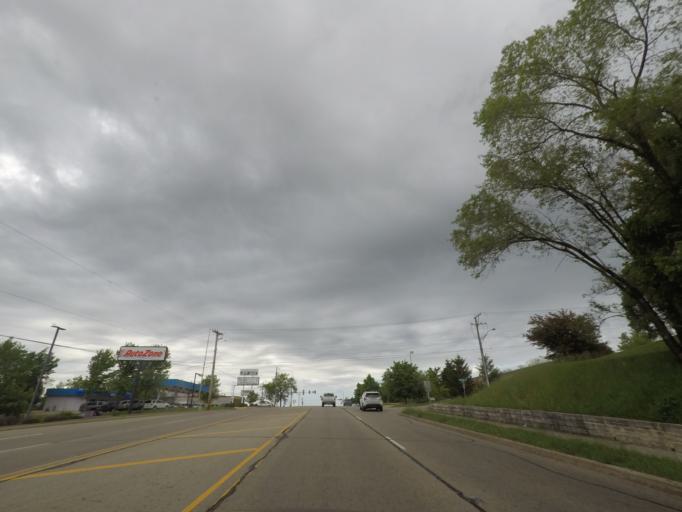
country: US
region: Illinois
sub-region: Winnebago County
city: Loves Park
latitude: 42.2625
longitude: -89.0291
